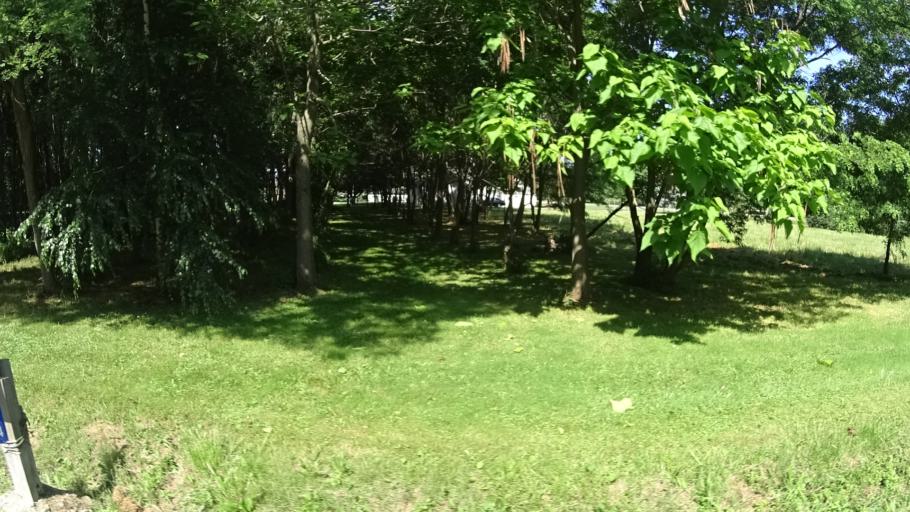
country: US
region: Ohio
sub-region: Erie County
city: Huron
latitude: 41.3838
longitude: -82.4585
